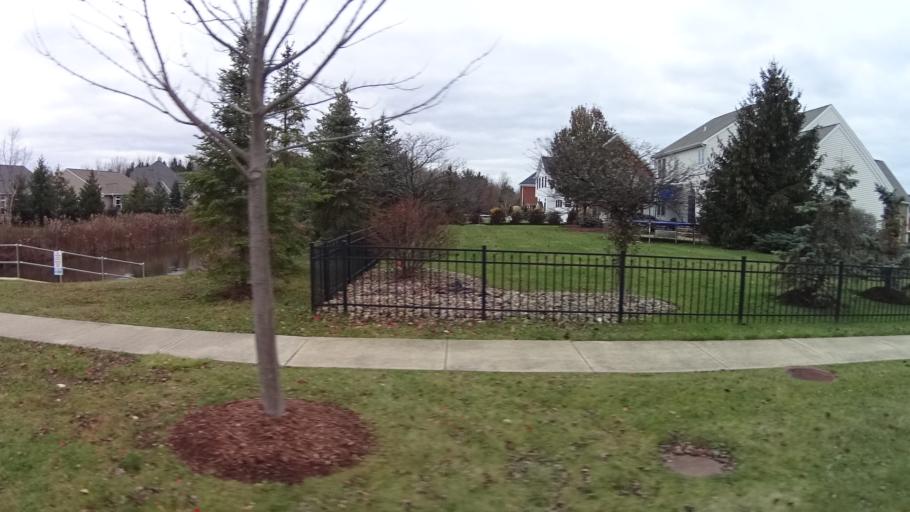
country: US
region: Ohio
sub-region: Lorain County
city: Avon Center
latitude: 41.4824
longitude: -81.9822
